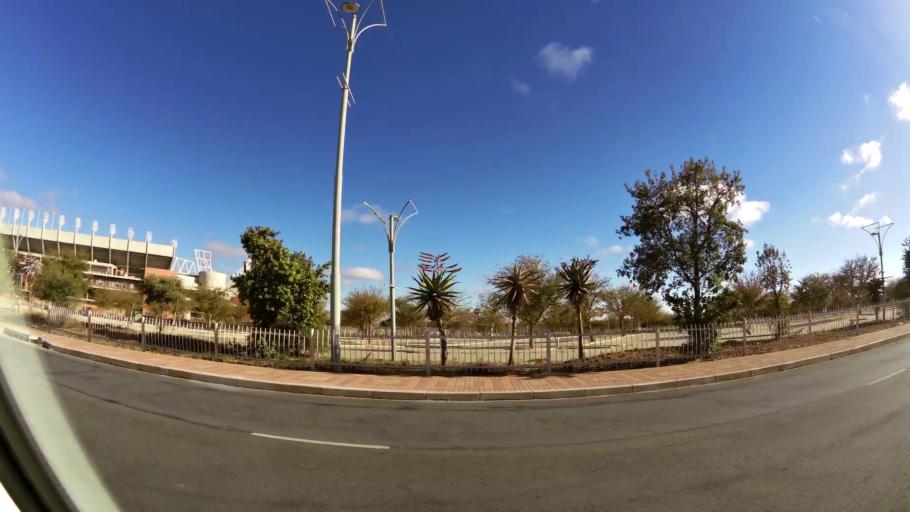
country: ZA
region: Limpopo
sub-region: Capricorn District Municipality
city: Polokwane
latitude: -23.9245
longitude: 29.4715
